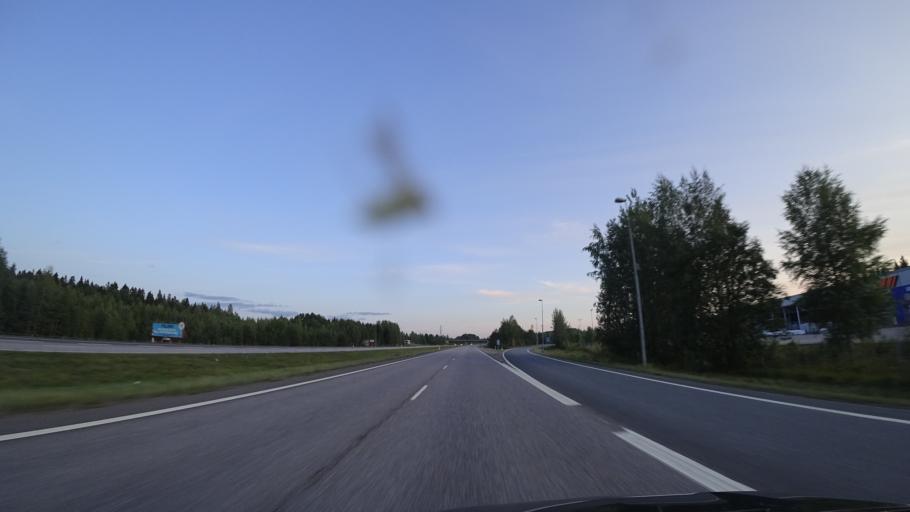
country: FI
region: Uusimaa
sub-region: Helsinki
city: Hyvinge
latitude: 60.6249
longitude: 24.8092
